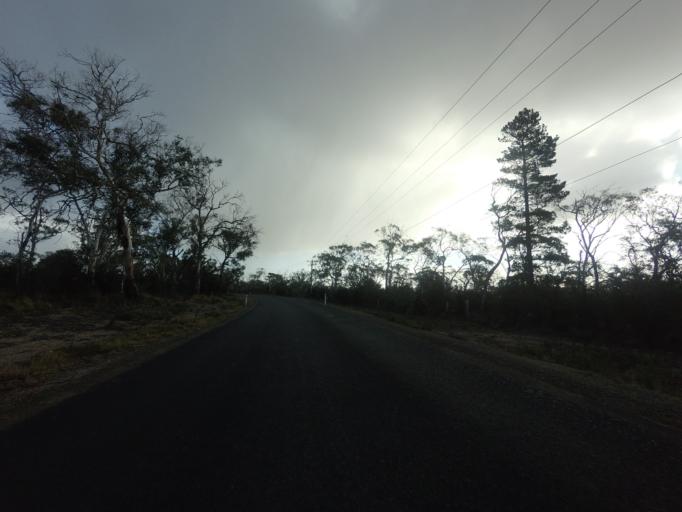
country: AU
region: Tasmania
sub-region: Break O'Day
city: St Helens
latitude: -42.0931
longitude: 148.1016
